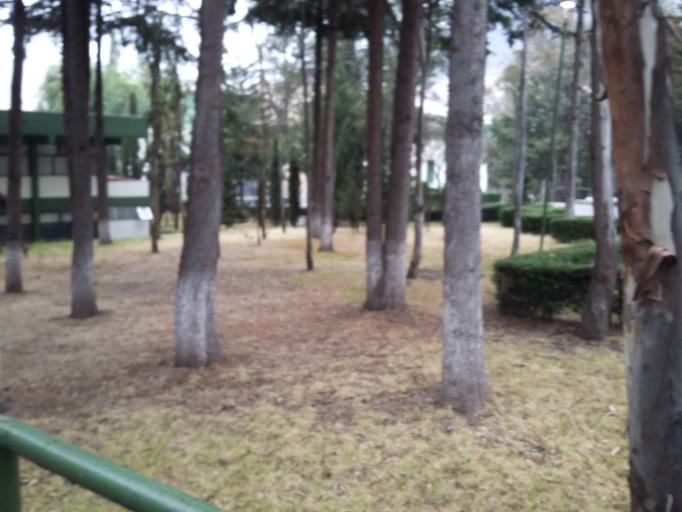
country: MX
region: Mexico
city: San Buenaventura
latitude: 19.2858
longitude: -99.6789
